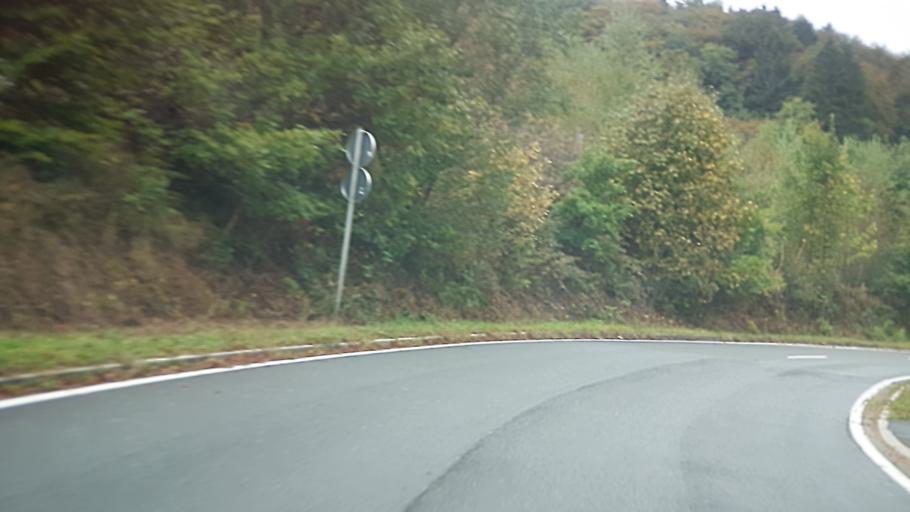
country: DE
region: North Rhine-Westphalia
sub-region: Regierungsbezirk Arnsberg
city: Luedenscheid
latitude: 51.1807
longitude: 7.6719
